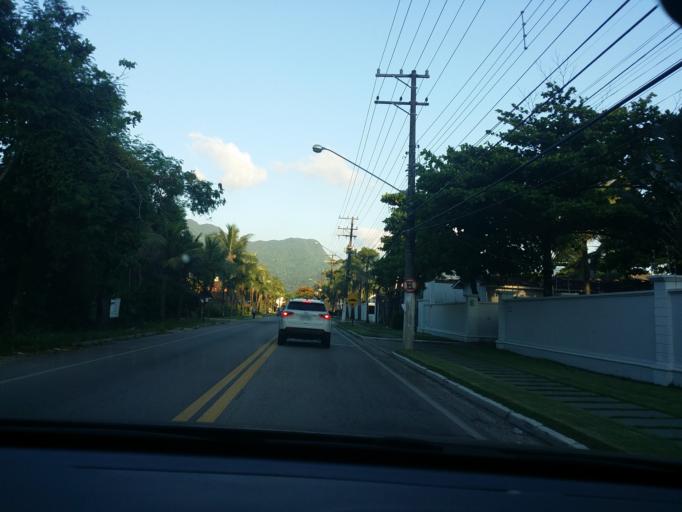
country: BR
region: Sao Paulo
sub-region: Sao Sebastiao
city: Sao Sebastiao
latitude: -23.7902
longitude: -45.5813
